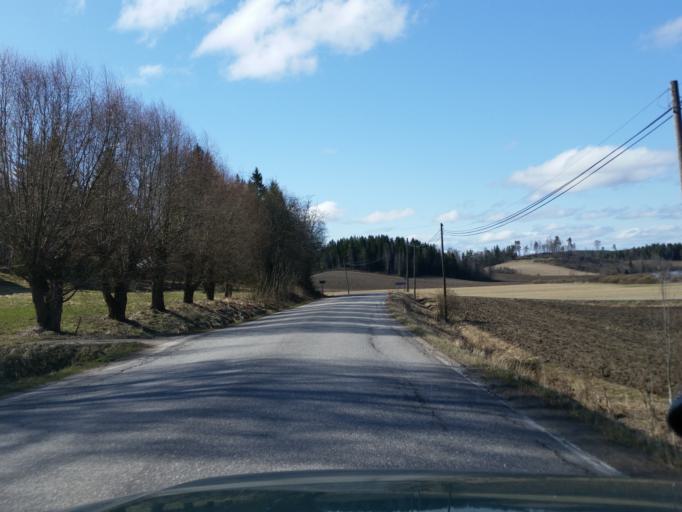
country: FI
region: Uusimaa
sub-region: Helsinki
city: Vihti
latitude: 60.4326
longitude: 24.2453
